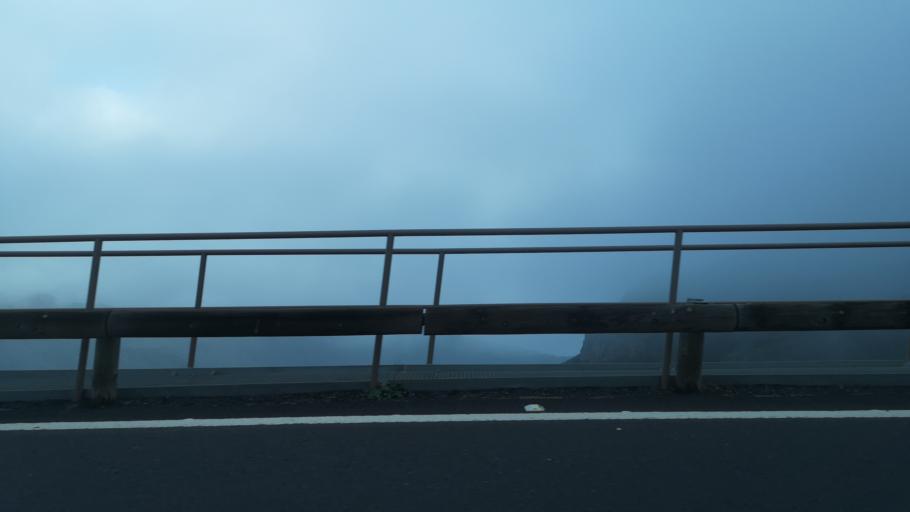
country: ES
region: Canary Islands
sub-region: Provincia de Santa Cruz de Tenerife
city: Alajero
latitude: 28.1044
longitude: -17.2095
